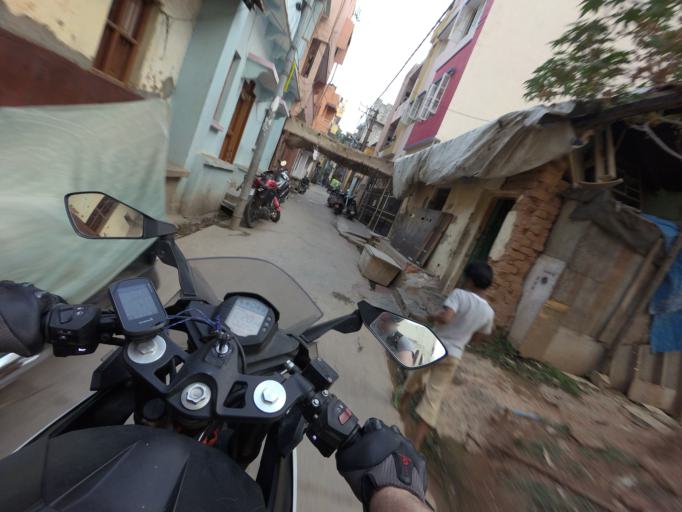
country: IN
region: Karnataka
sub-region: Bangalore Urban
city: Bangalore
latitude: 12.9744
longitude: 77.6221
